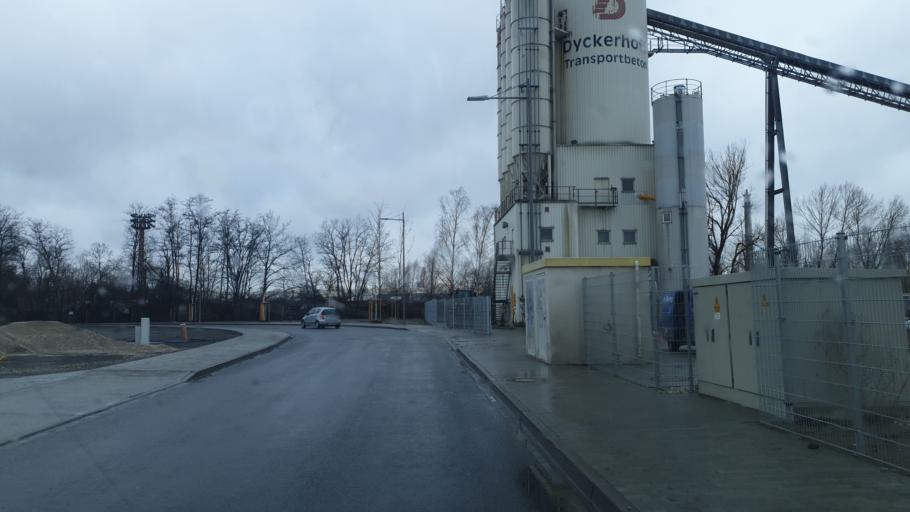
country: DE
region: Saxony
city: Taucha
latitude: 51.3396
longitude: 12.4722
